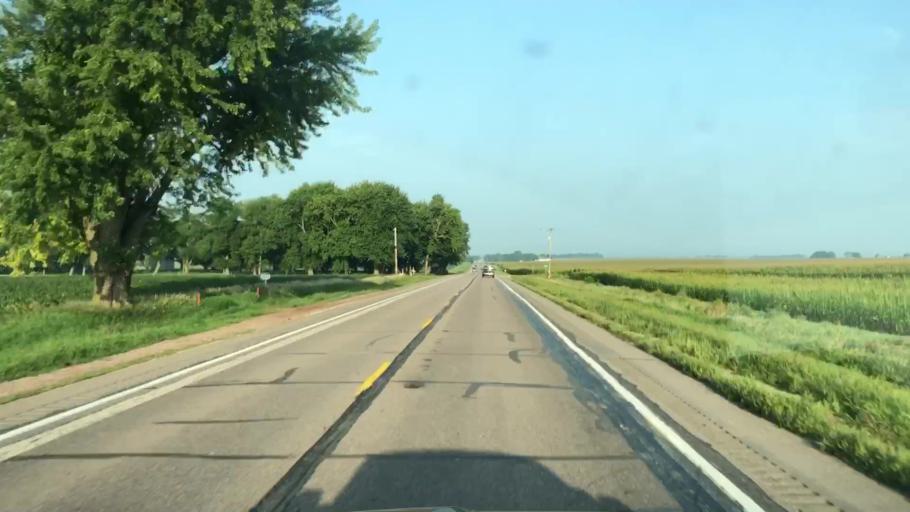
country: US
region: Iowa
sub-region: O'Brien County
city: Sheldon
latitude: 43.1860
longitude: -95.8996
